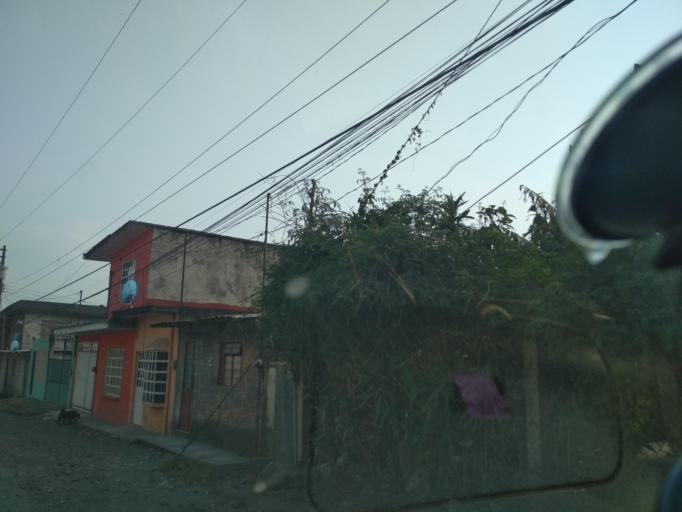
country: MX
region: Veracruz
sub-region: Ixhuatlancillo
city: Fraccionamiento Valle Dorado
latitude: 18.8651
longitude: -97.1169
